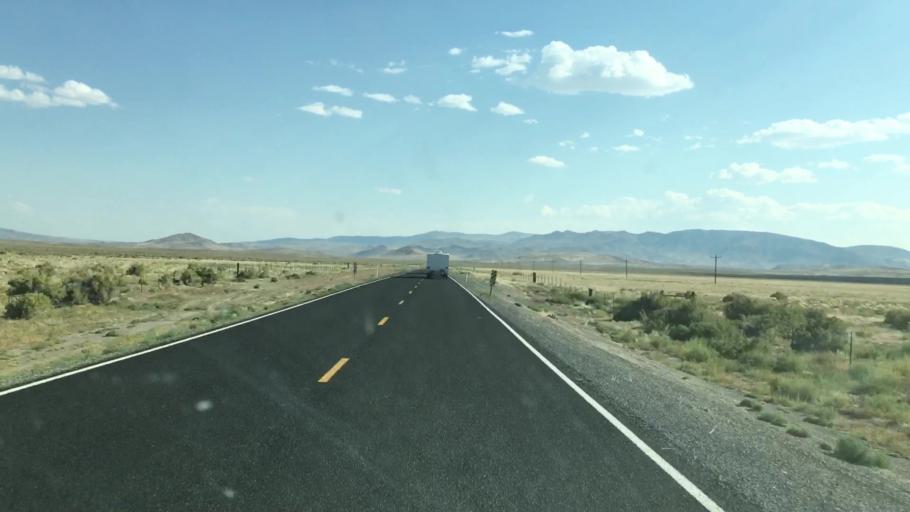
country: US
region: Nevada
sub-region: Lyon County
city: Fernley
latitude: 39.6839
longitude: -119.3348
